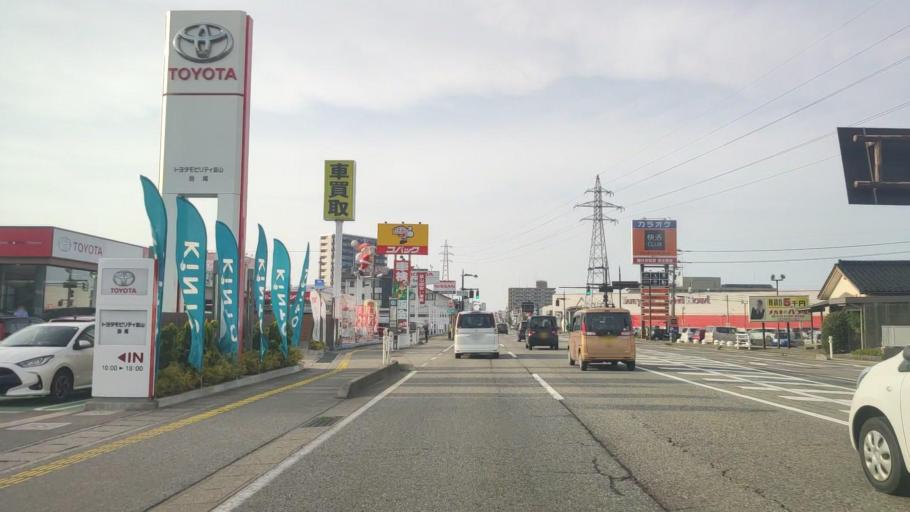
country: JP
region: Toyama
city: Toyama-shi
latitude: 36.6677
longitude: 137.2101
